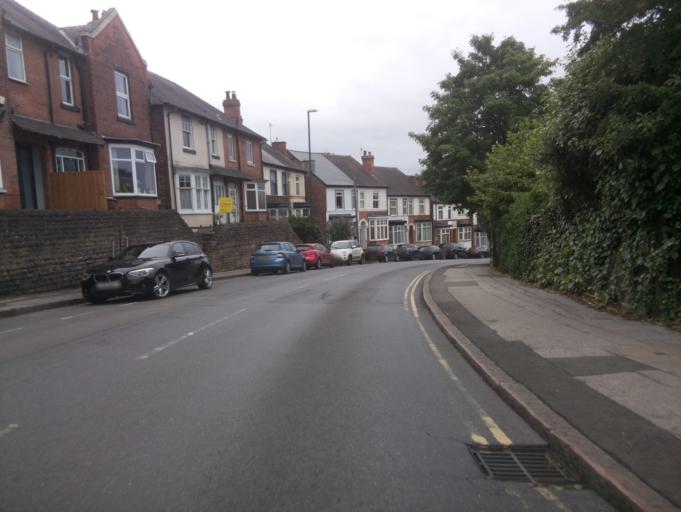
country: GB
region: England
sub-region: Nottinghamshire
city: Arnold
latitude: 52.9808
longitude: -1.1401
